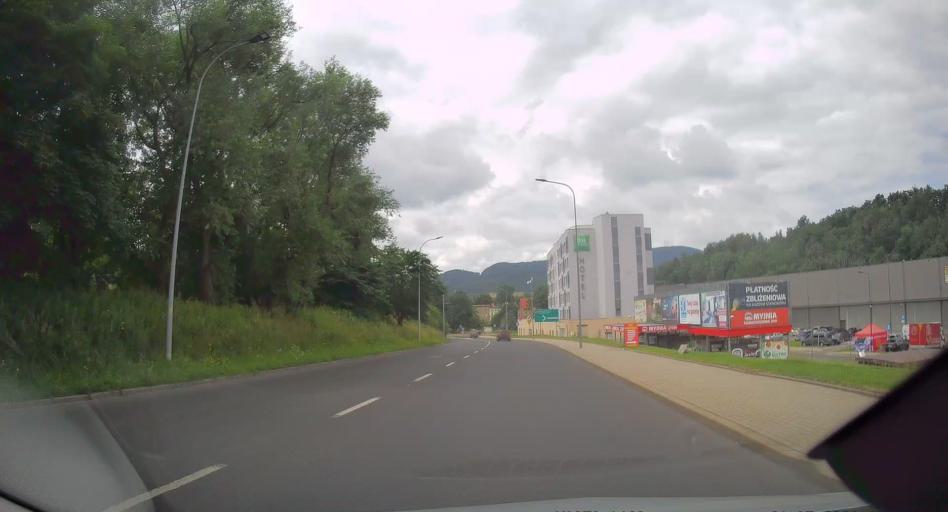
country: PL
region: Lower Silesian Voivodeship
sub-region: Powiat walbrzyski
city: Walbrzych
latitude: 50.7653
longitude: 16.2638
